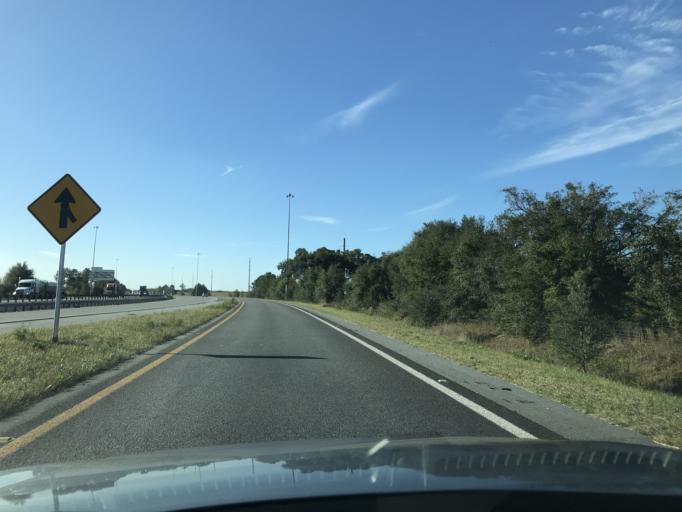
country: US
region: Florida
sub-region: Sumter County
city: Lake Panasoffkee
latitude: 28.7503
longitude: -82.1053
